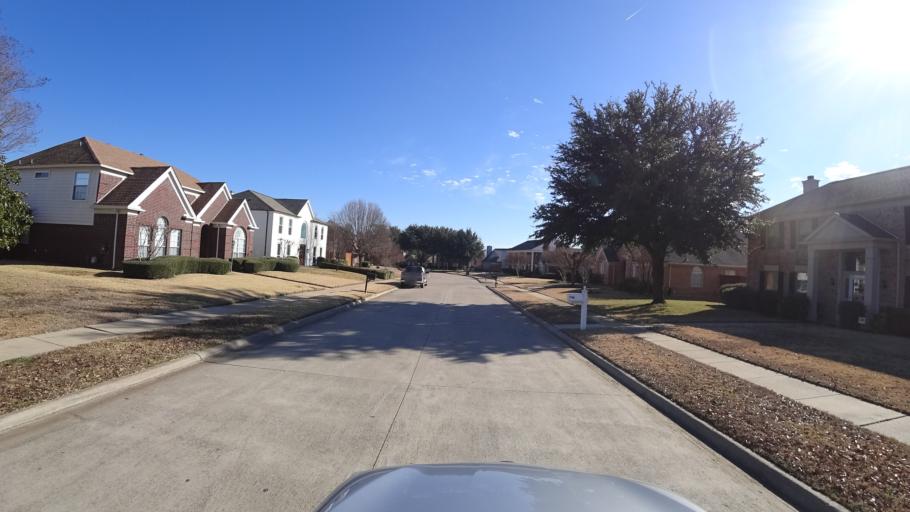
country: US
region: Texas
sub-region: Denton County
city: Lewisville
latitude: 33.0173
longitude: -97.0329
